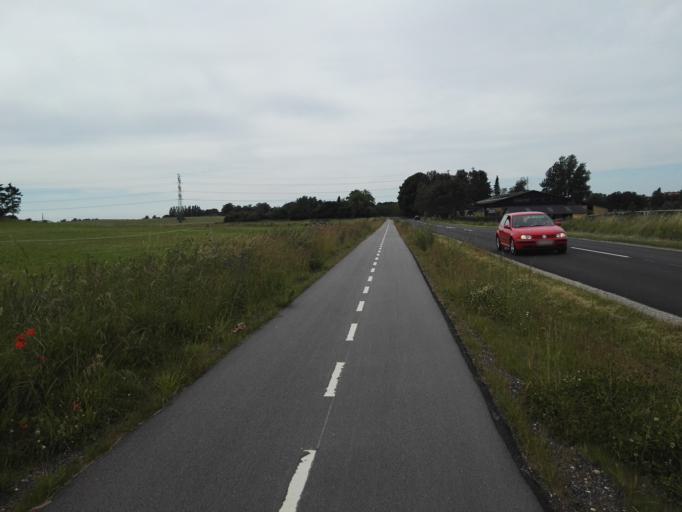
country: DK
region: Capital Region
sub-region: Hillerod Kommune
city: Skaevinge
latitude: 55.9148
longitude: 12.1765
